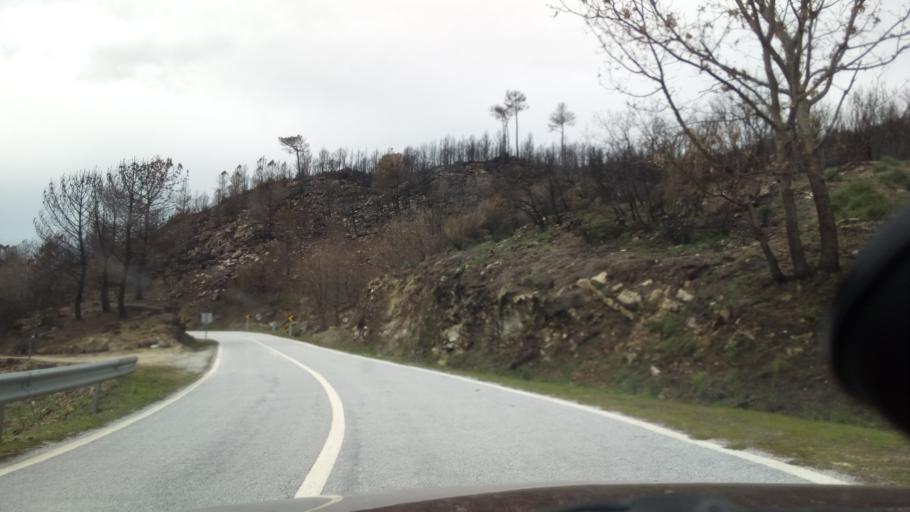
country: PT
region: Guarda
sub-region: Manteigas
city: Manteigas
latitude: 40.4696
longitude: -7.5877
